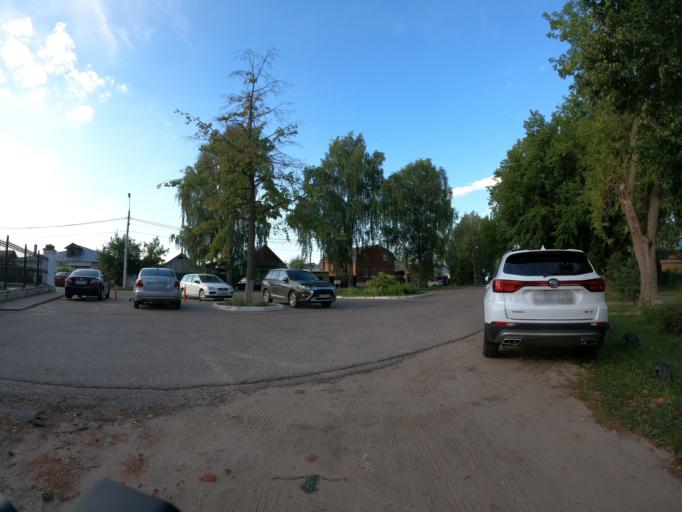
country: RU
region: Moskovskaya
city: Raduzhnyy
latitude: 55.1000
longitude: 38.7260
